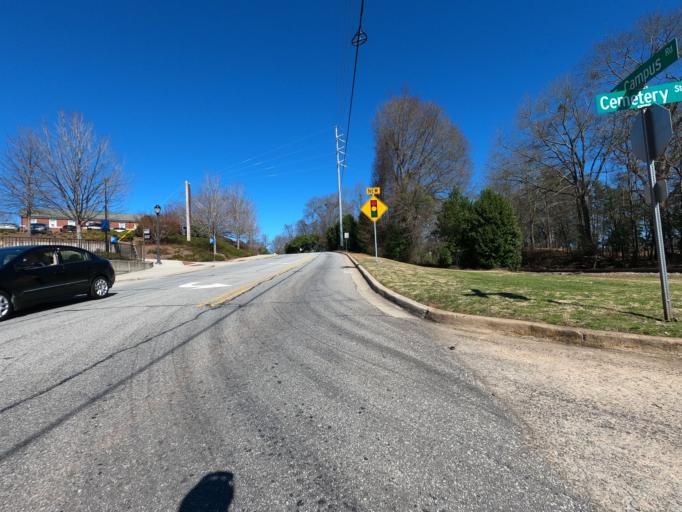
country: US
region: Georgia
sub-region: Clarke County
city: Athens
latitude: 33.9506
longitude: -83.3715
